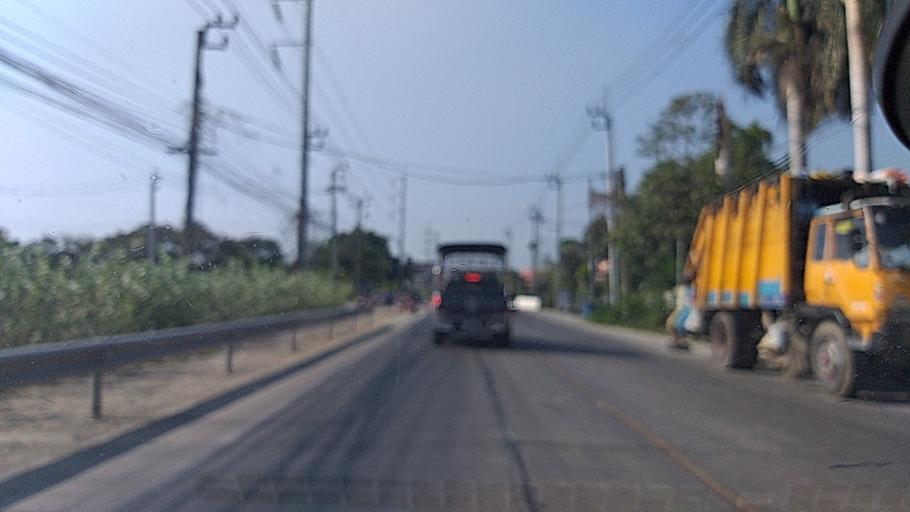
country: TH
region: Nonthaburi
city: Sai Noi
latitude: 13.9149
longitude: 100.3221
